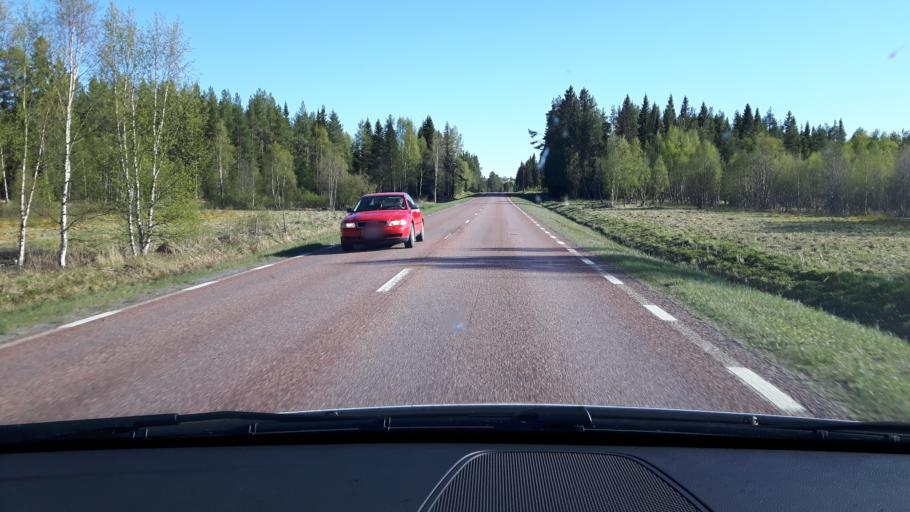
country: SE
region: Jaemtland
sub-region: Stroemsunds Kommun
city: Stroemsund
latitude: 63.7539
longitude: 15.4976
